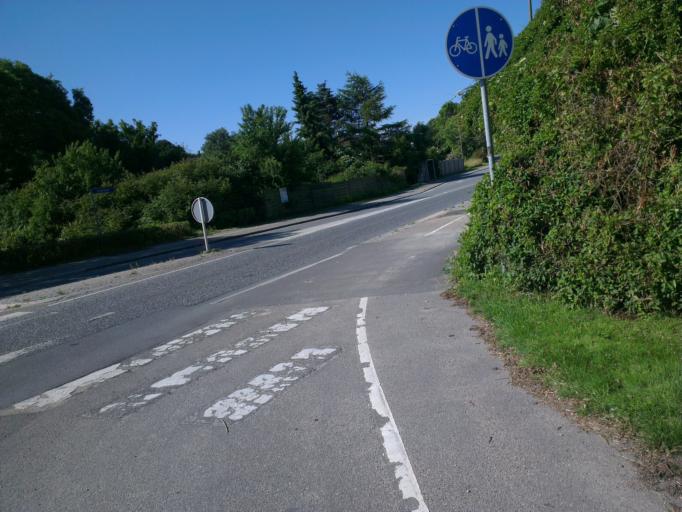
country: DK
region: Capital Region
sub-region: Frederikssund Kommune
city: Jaegerspris
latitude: 55.8071
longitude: 11.9827
